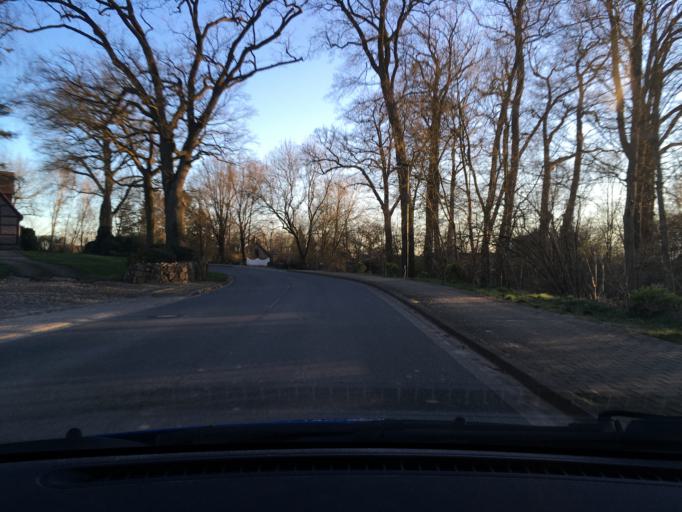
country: DE
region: Lower Saxony
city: Dahlem
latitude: 53.1886
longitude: 10.7533
